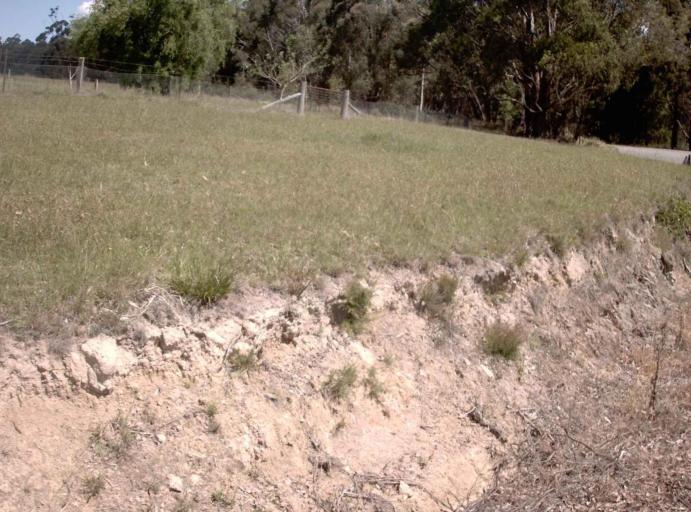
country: AU
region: New South Wales
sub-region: Bombala
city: Bombala
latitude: -37.1773
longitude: 148.6970
